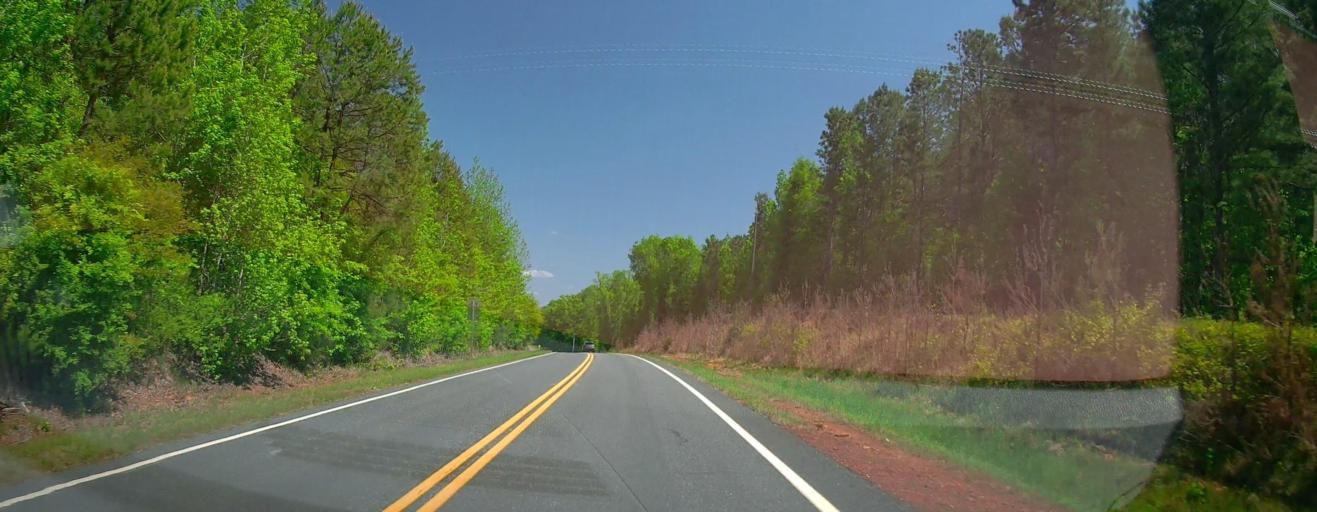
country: US
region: Georgia
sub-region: Jasper County
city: Monticello
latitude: 33.2361
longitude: -83.5468
